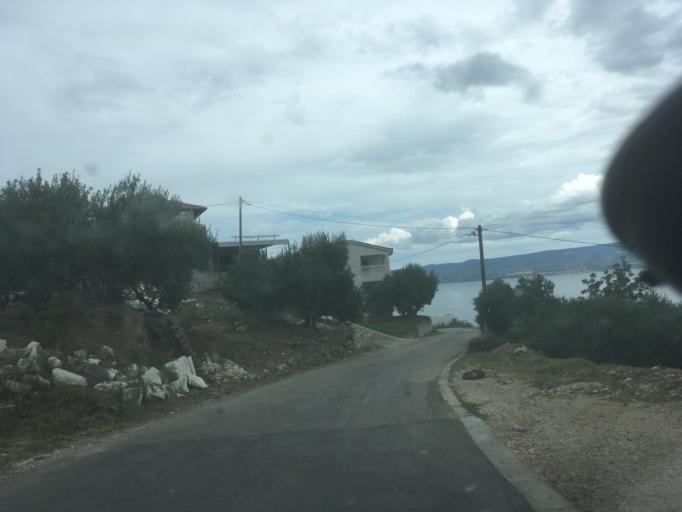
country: HR
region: Splitsko-Dalmatinska
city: Jesenice
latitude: 43.4575
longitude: 16.6205
